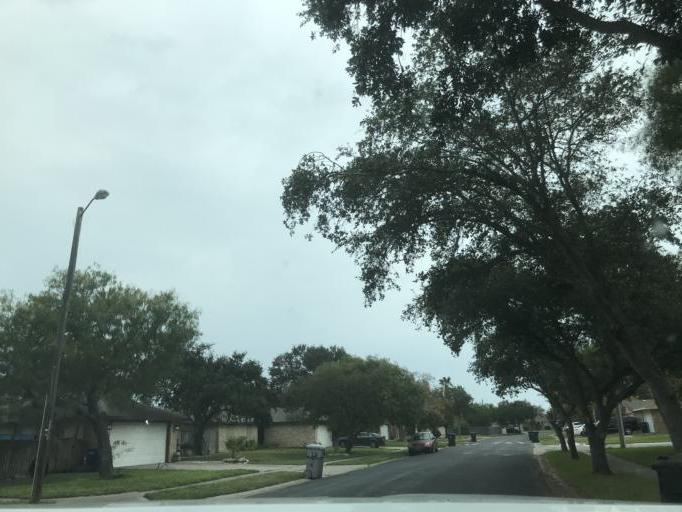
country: US
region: Texas
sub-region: Nueces County
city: Corpus Christi
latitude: 27.6717
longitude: -97.3484
